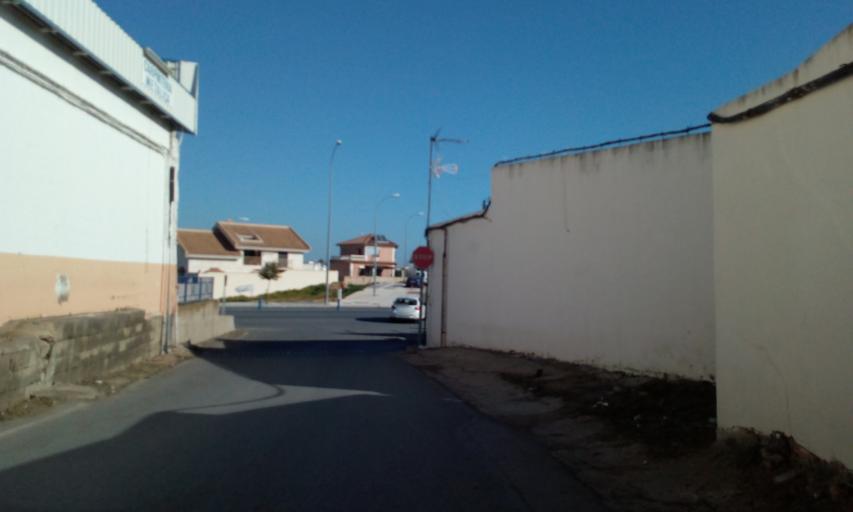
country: ES
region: Andalusia
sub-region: Provincia de Huelva
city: Lepe
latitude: 37.2520
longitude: -7.2095
